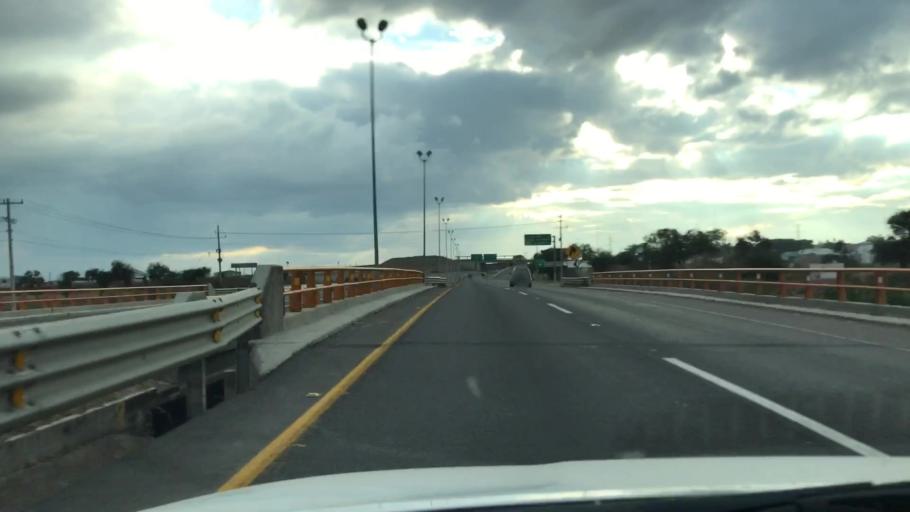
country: MX
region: Guanajuato
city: Penjamo
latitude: 20.4243
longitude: -101.7119
